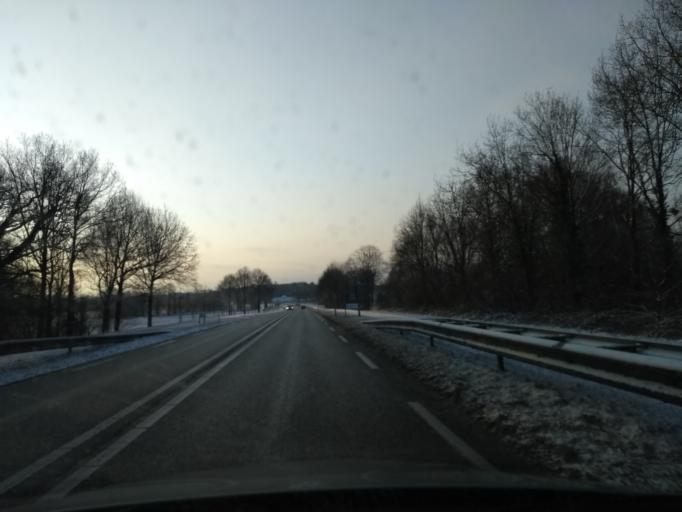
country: NL
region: Overijssel
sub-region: Gemeente Almelo
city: Almelo
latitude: 52.2959
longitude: 6.6597
